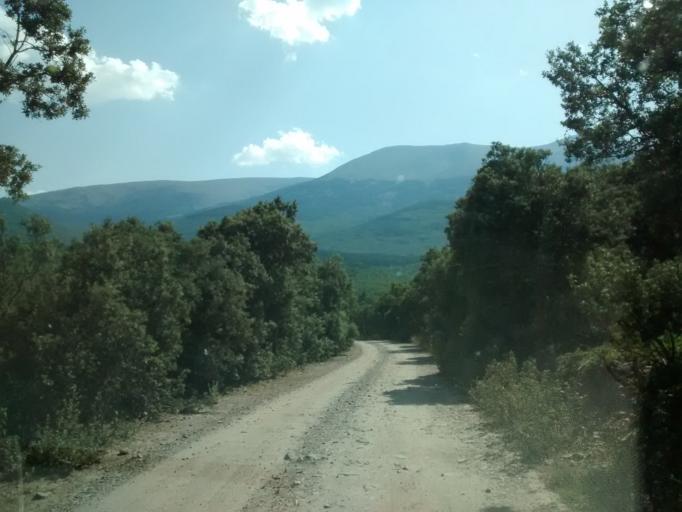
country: ES
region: Aragon
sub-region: Provincia de Zaragoza
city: Lituenigo
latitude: 41.8158
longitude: -1.7902
